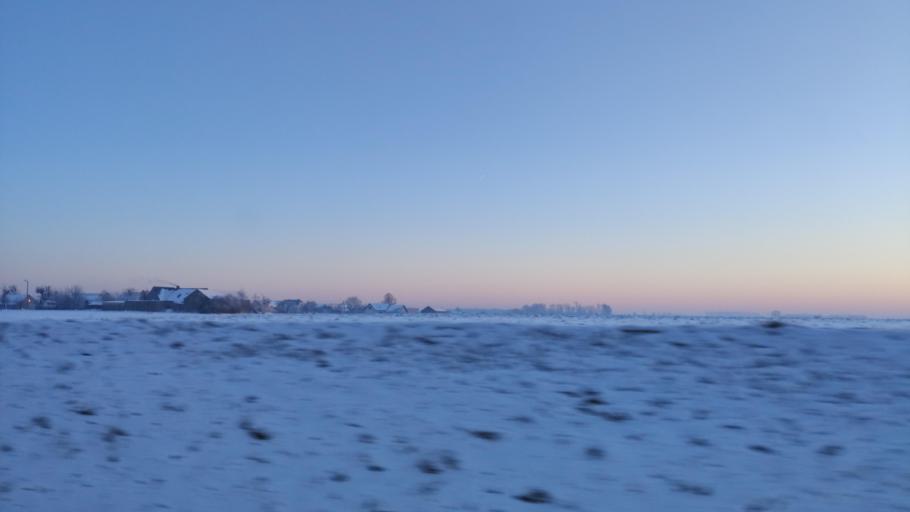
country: PL
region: Kujawsko-Pomorskie
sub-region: Powiat zninski
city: Barcin
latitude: 52.8712
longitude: 17.8333
